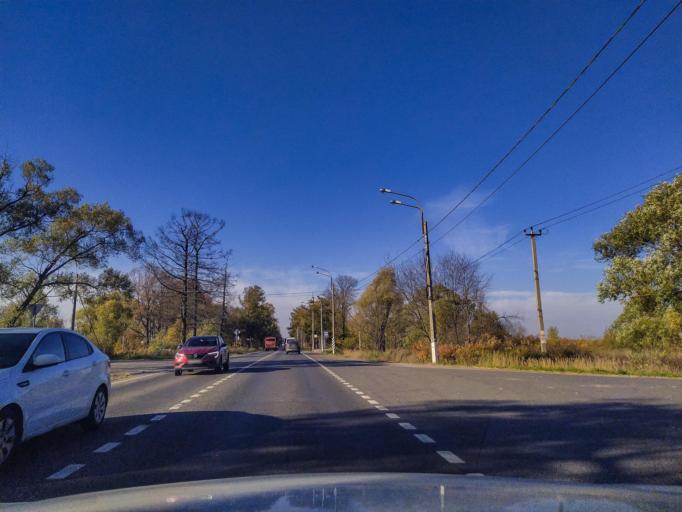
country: RU
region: St.-Petersburg
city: Aleksandrovskaya
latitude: 59.7049
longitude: 30.3438
